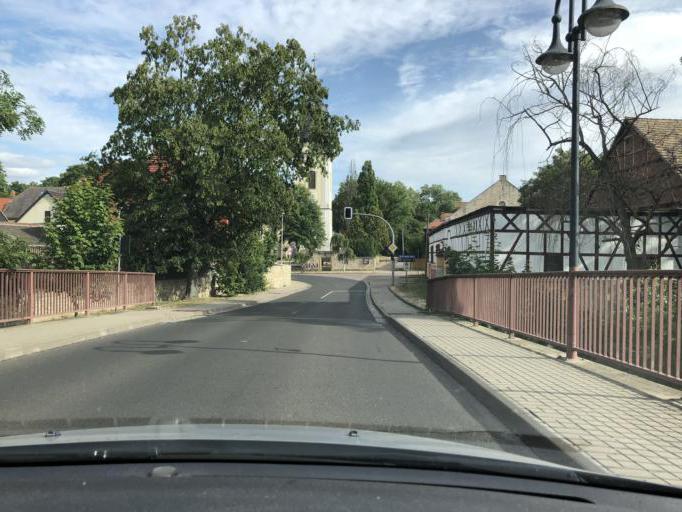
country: DE
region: Thuringia
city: Niederrossla
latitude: 51.0375
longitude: 11.4856
